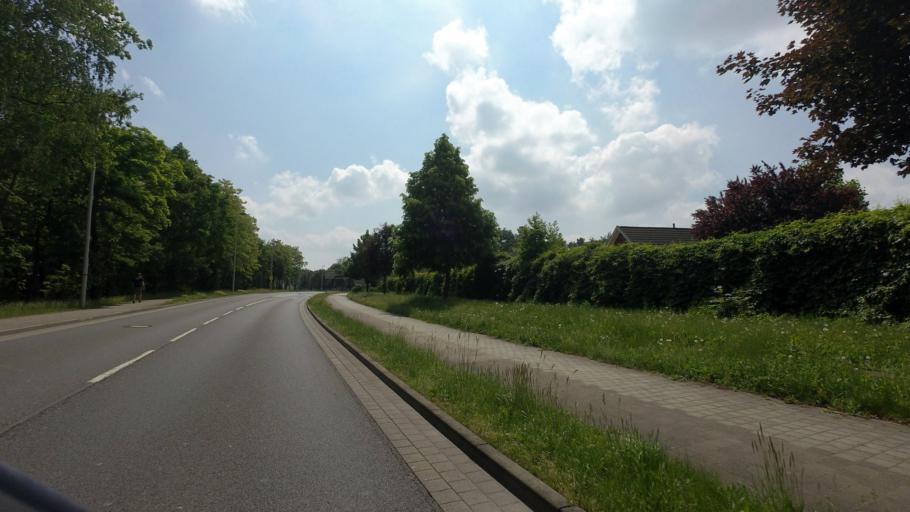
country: DE
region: Brandenburg
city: Cottbus
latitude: 51.7046
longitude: 14.3613
